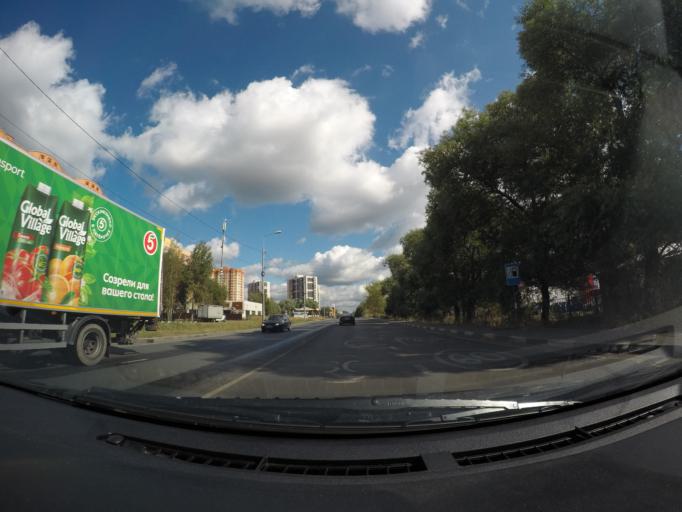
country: RU
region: Moskovskaya
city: Ramenskoye
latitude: 55.5904
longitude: 38.2530
